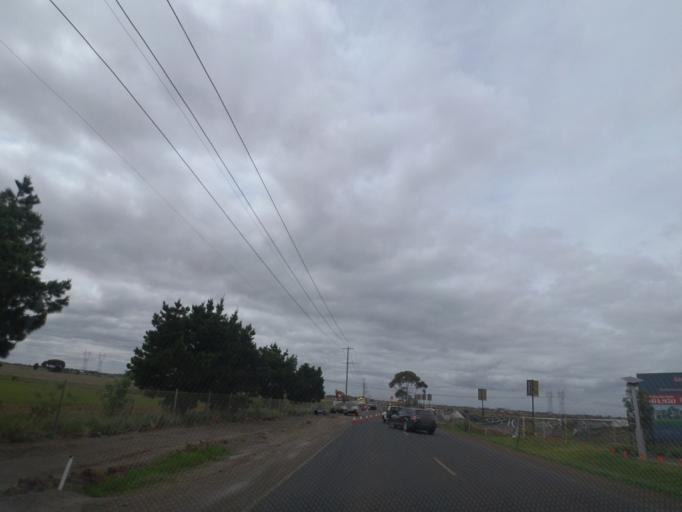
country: AU
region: Victoria
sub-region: Melton
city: Caroline Springs
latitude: -37.7191
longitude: 144.7132
